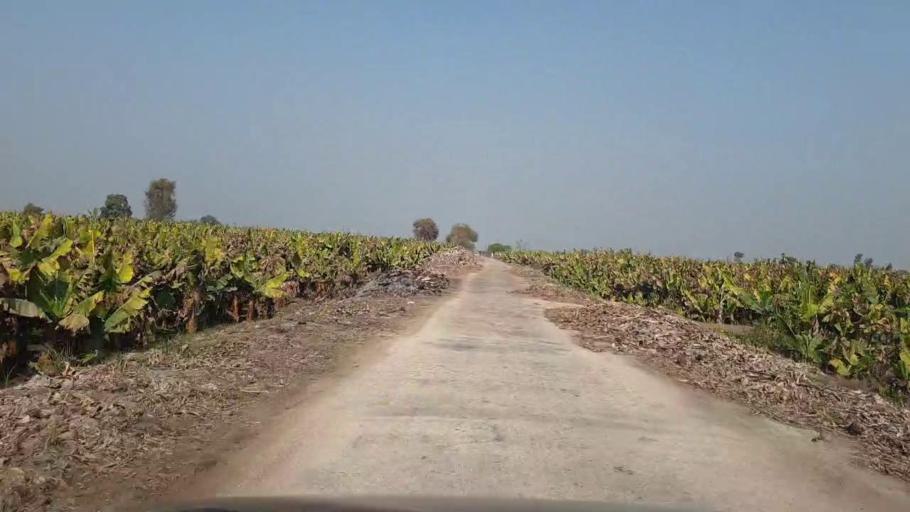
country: PK
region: Sindh
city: Bhit Shah
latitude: 25.7710
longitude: 68.4942
